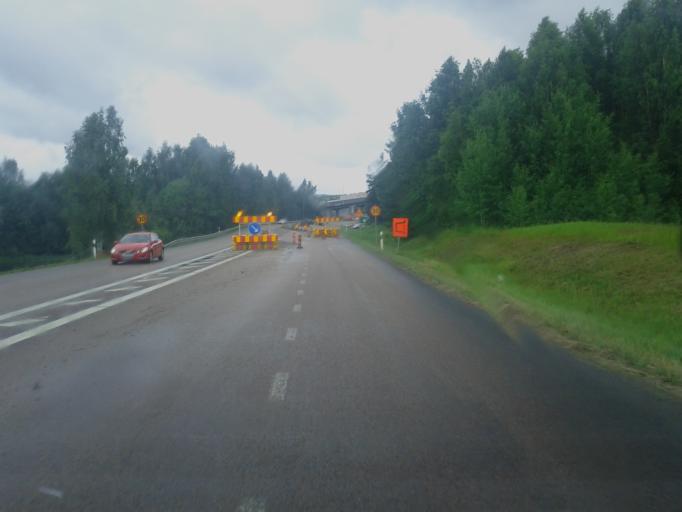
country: SE
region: Vaesternorrland
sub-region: Sundsvalls Kommun
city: Sundsvall
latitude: 62.4054
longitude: 17.2335
